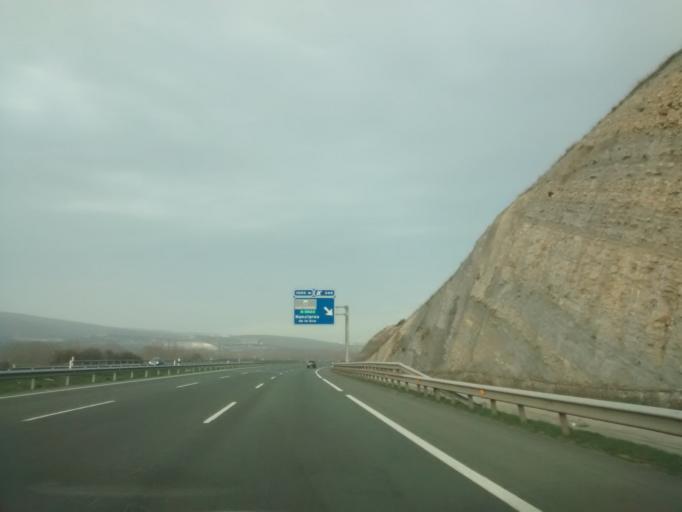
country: ES
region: Basque Country
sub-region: Provincia de Alava
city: Arminon
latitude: 42.7953
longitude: -2.8204
